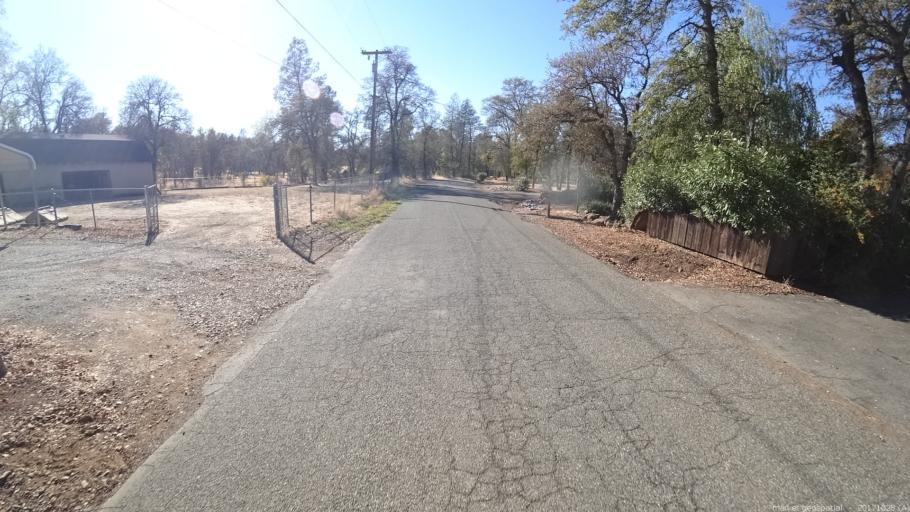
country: US
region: California
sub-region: Shasta County
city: Central Valley (historical)
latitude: 40.6367
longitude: -122.3737
